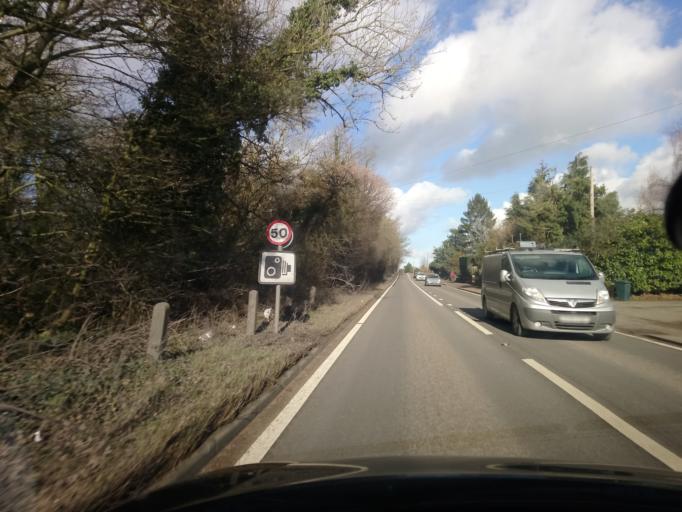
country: GB
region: England
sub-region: Shropshire
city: Astley
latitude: 52.7560
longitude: -2.7165
